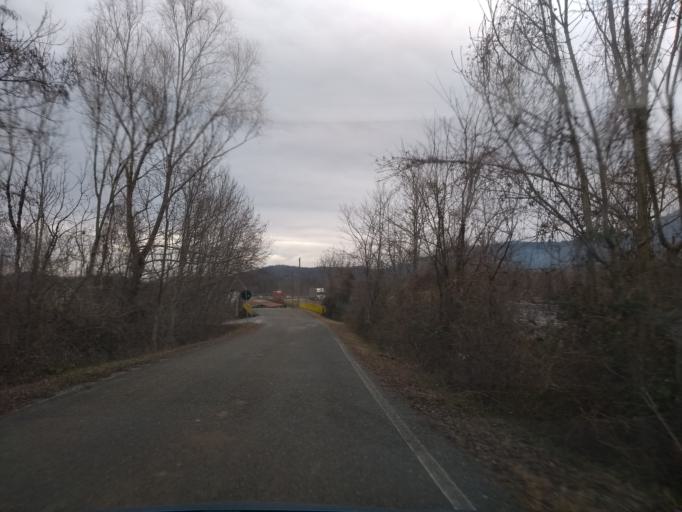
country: IT
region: Piedmont
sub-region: Provincia di Torino
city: Lessolo
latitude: 45.4952
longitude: 7.8313
